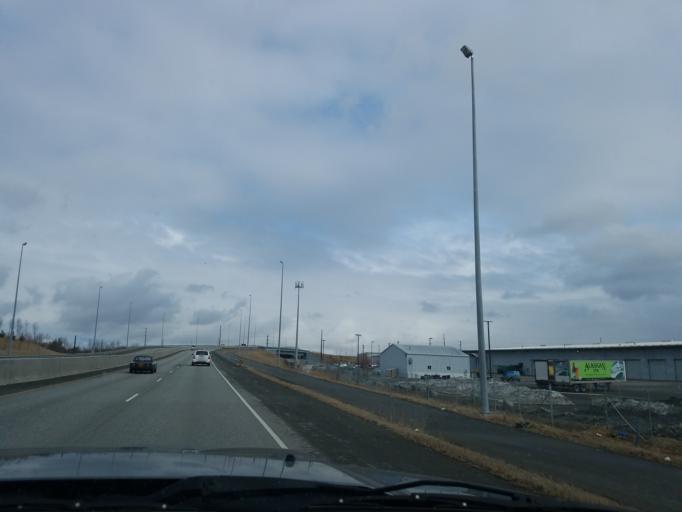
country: US
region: Alaska
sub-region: Anchorage Municipality
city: Anchorage
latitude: 61.1622
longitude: -149.8995
